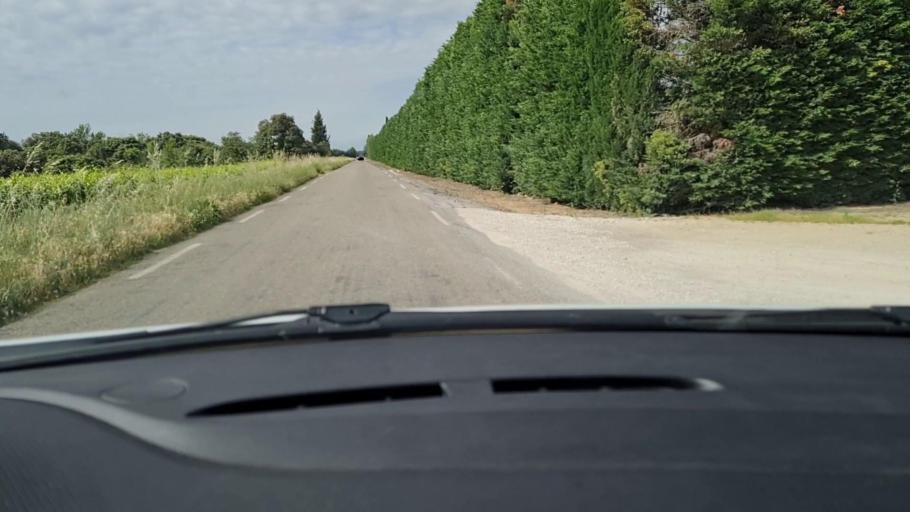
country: FR
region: Languedoc-Roussillon
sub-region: Departement du Gard
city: Jonquieres-Saint-Vincent
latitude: 43.8130
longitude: 4.5479
